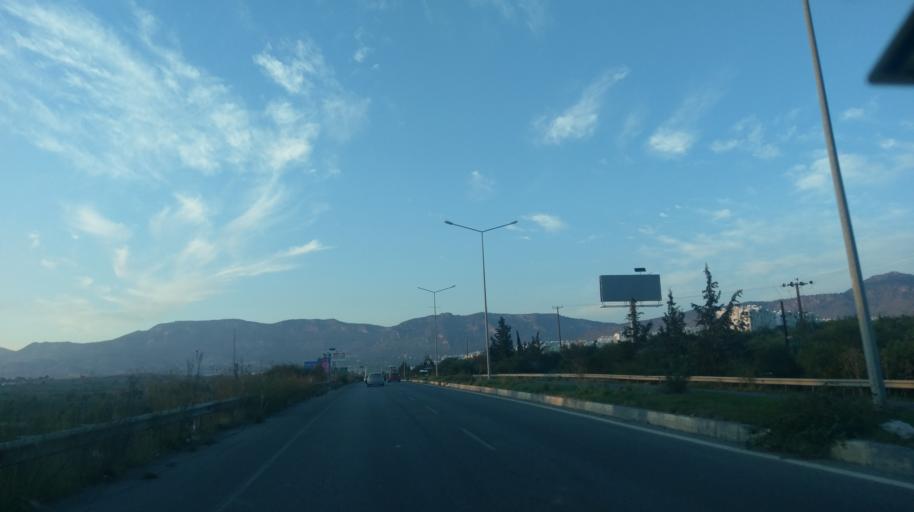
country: CY
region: Keryneia
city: Kyrenia
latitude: 35.2519
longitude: 33.3028
